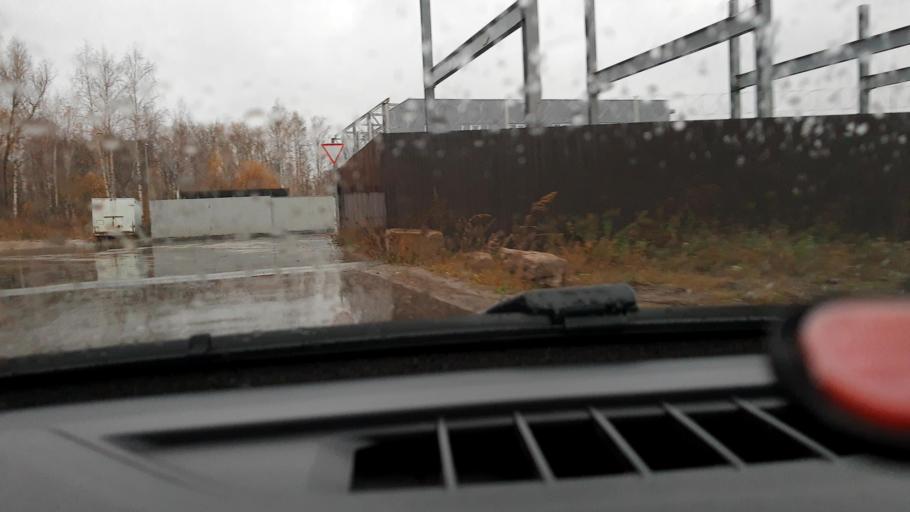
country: RU
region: Nizjnij Novgorod
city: Gorbatovka
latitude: 56.3161
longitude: 43.8504
